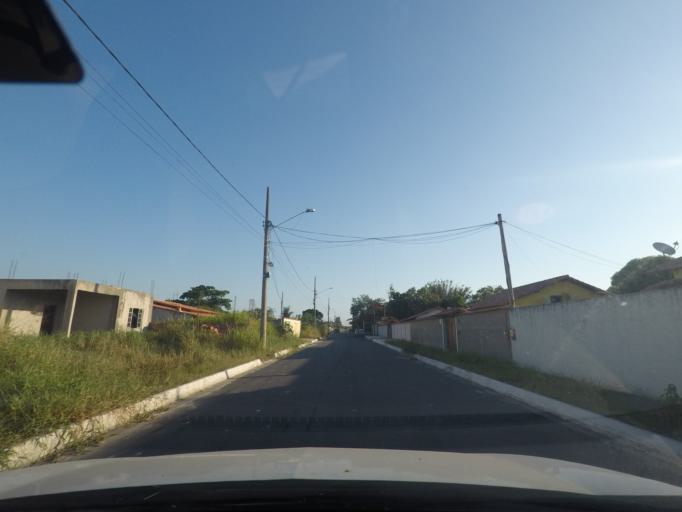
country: BR
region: Rio de Janeiro
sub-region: Marica
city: Marica
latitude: -22.9567
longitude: -42.9326
